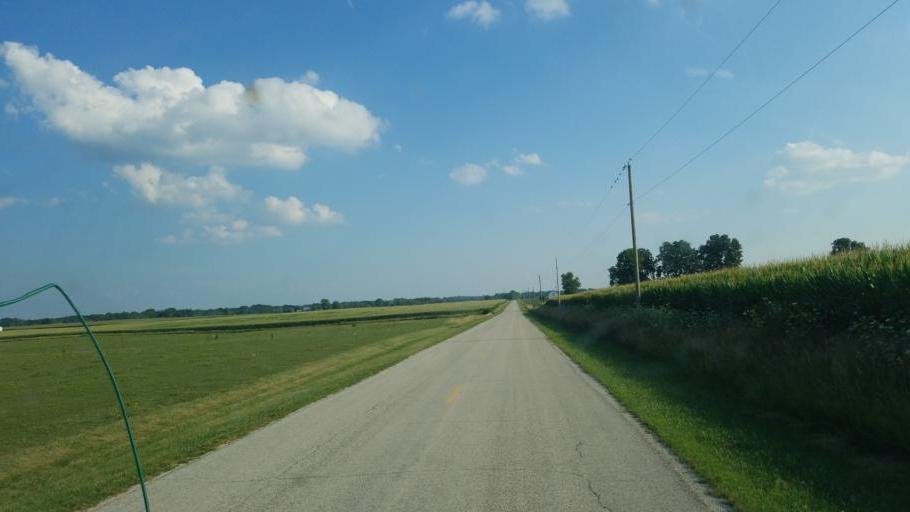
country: US
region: Ohio
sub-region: Crawford County
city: Bucyrus
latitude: 40.8513
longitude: -82.9018
